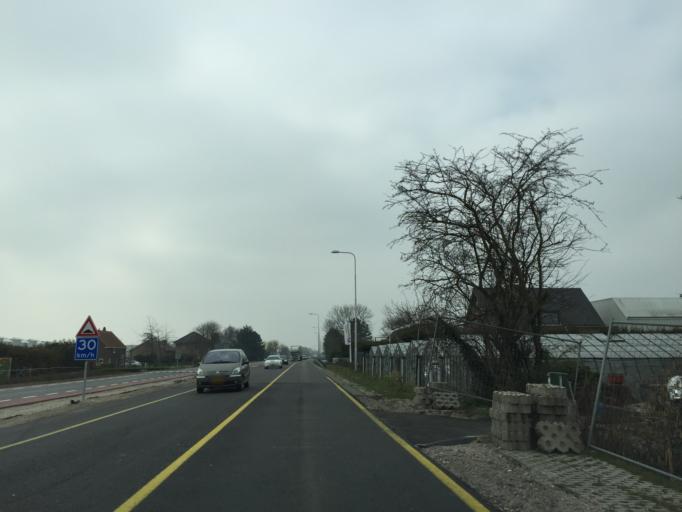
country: NL
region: South Holland
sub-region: Gemeente Westland
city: De Lier
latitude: 51.9769
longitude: 4.2637
